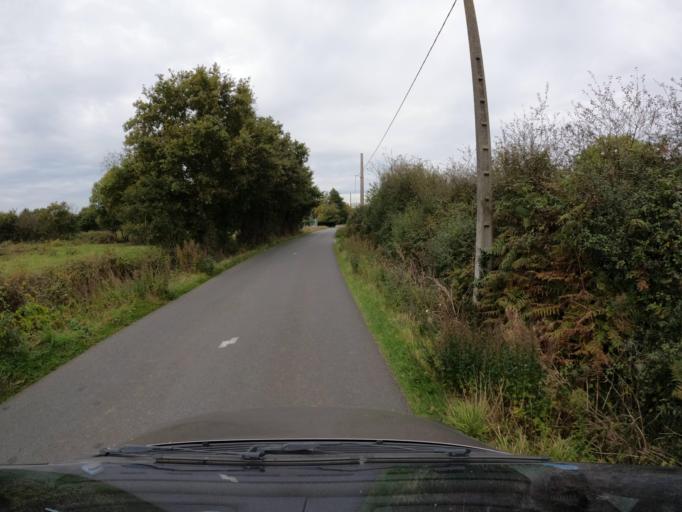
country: FR
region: Pays de la Loire
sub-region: Departement de Maine-et-Loire
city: La Seguiniere
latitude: 47.0532
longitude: -0.9402
